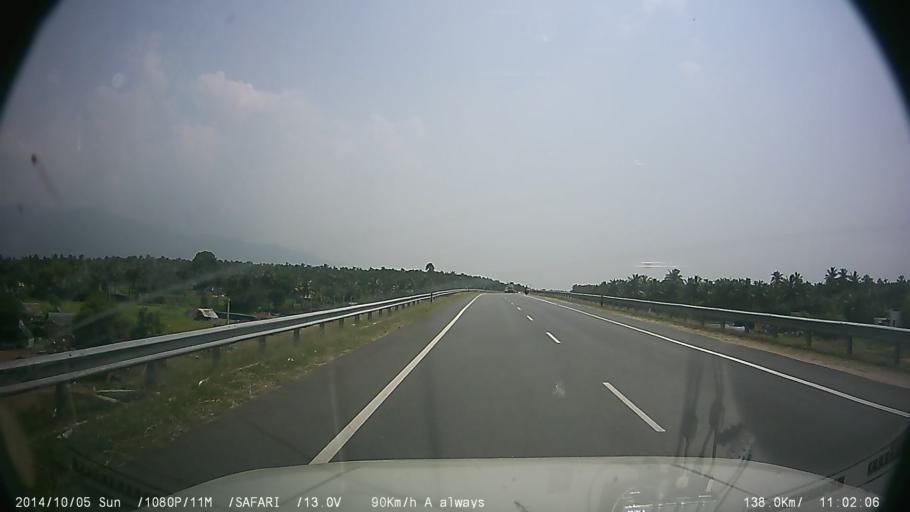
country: IN
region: Tamil Nadu
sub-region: Salem
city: Attur
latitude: 11.6140
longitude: 78.5680
